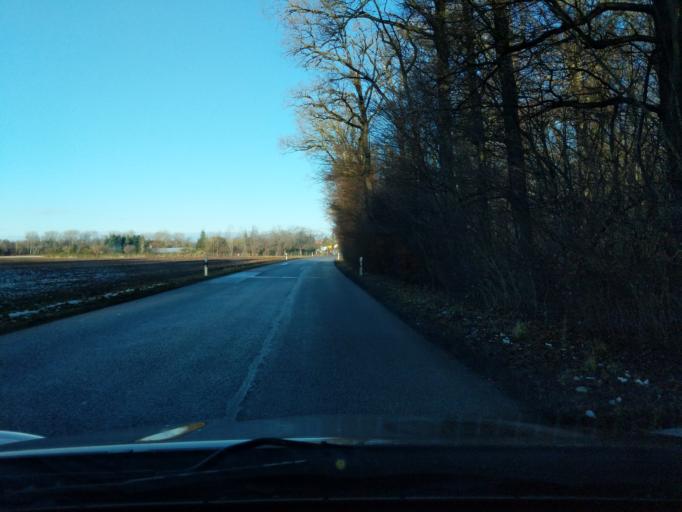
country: DE
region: Bavaria
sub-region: Upper Bavaria
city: Zorneding
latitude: 48.0889
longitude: 11.8469
